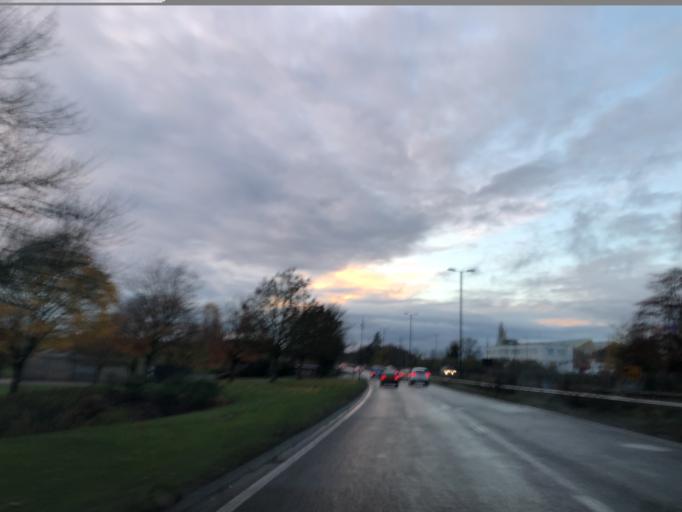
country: GB
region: England
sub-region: Coventry
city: Keresley
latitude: 52.4274
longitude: -1.5761
